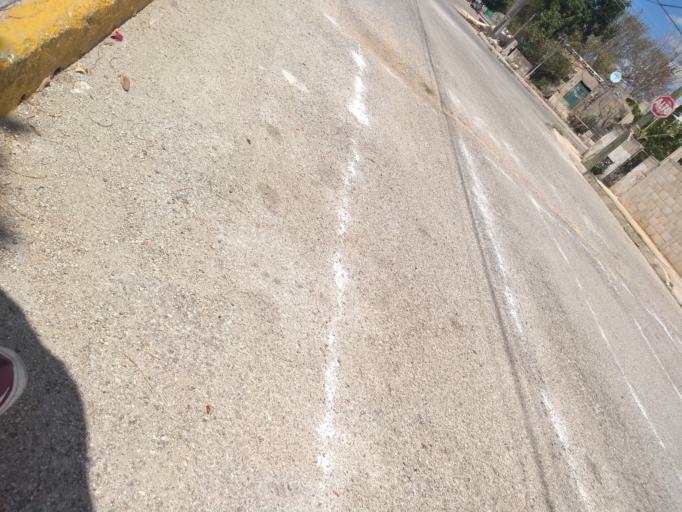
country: MX
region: Yucatan
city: Itzincab Palomeque
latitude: 20.9326
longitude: -89.6673
